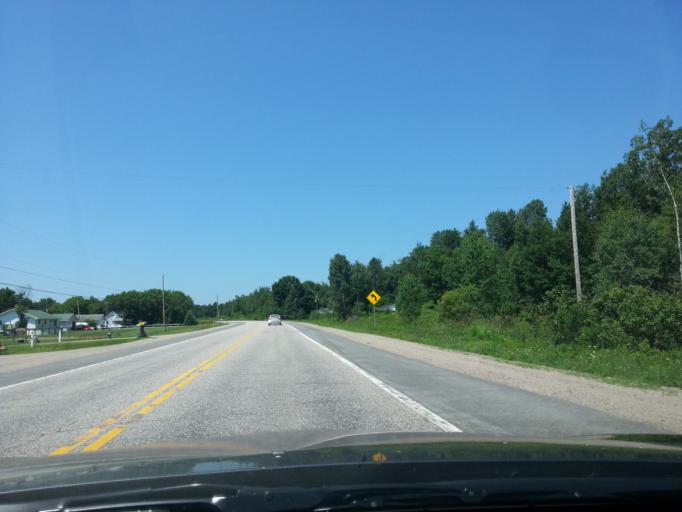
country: CA
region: Ontario
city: Arnprior
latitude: 45.5559
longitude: -76.1484
